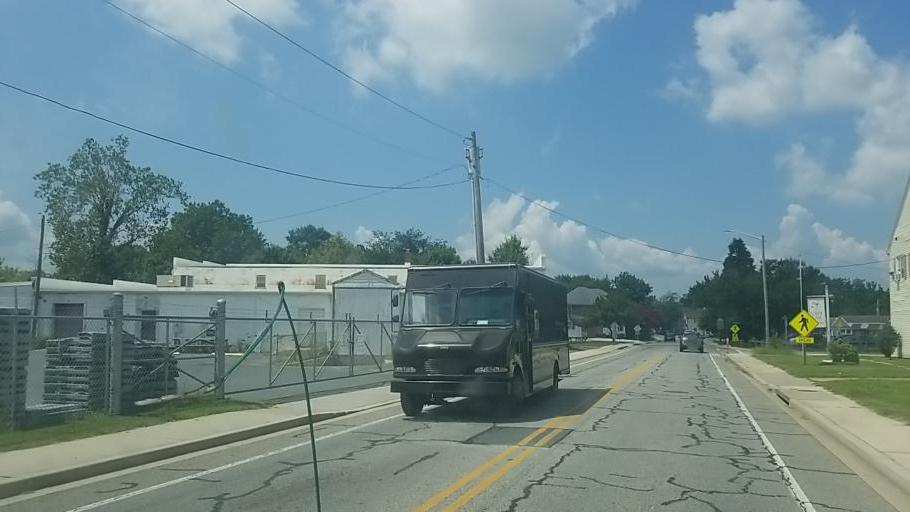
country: US
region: Maryland
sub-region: Talbot County
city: Easton
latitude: 38.7738
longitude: -76.0674
